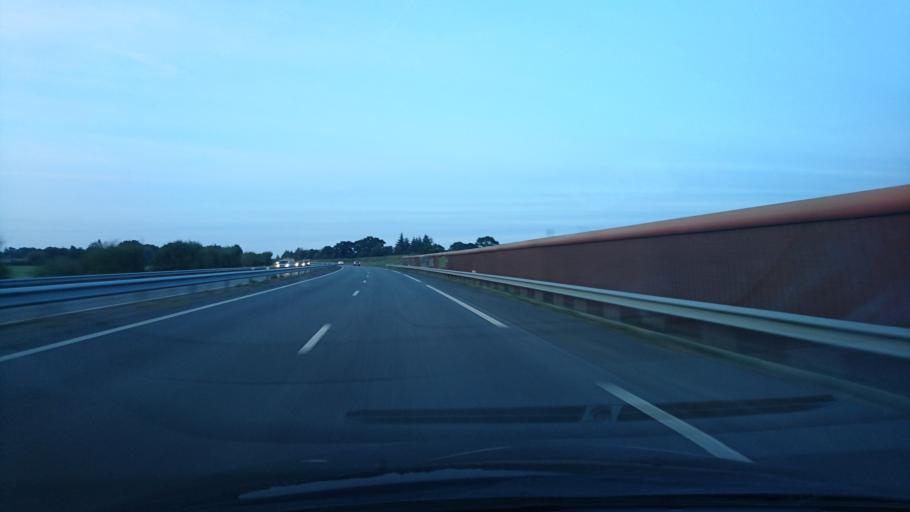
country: FR
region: Brittany
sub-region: Departement d'Ille-et-Vilaine
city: Guichen
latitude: 47.9538
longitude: -1.8172
